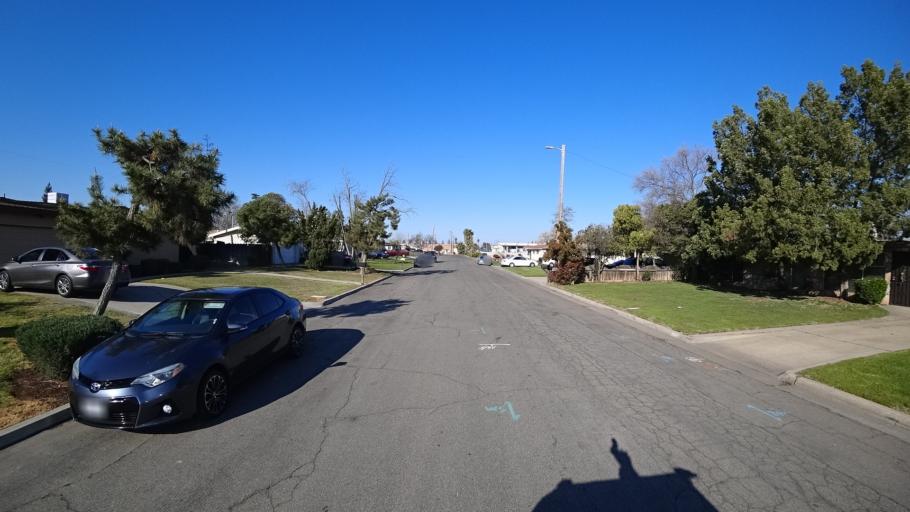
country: US
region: California
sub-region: Fresno County
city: Fresno
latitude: 36.8248
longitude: -119.7870
